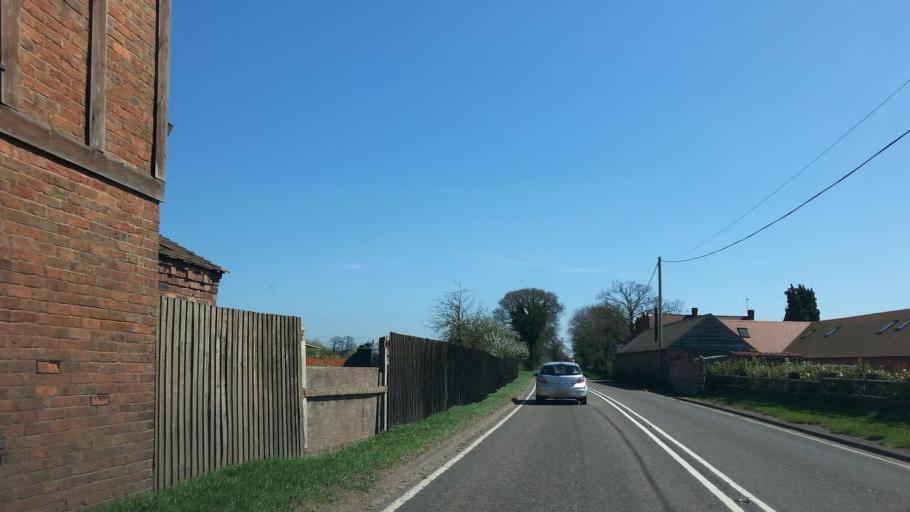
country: GB
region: England
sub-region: Staffordshire
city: Wheaton Aston
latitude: 52.6940
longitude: -2.2240
